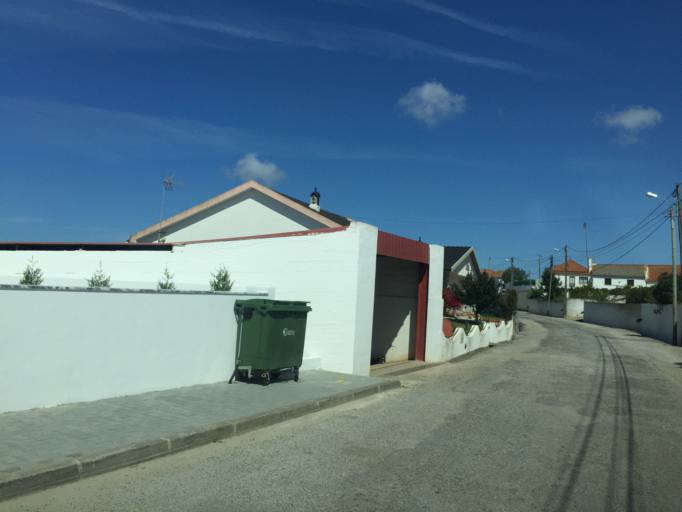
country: PT
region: Lisbon
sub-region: Lourinha
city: Lourinha
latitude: 39.2666
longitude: -9.3102
